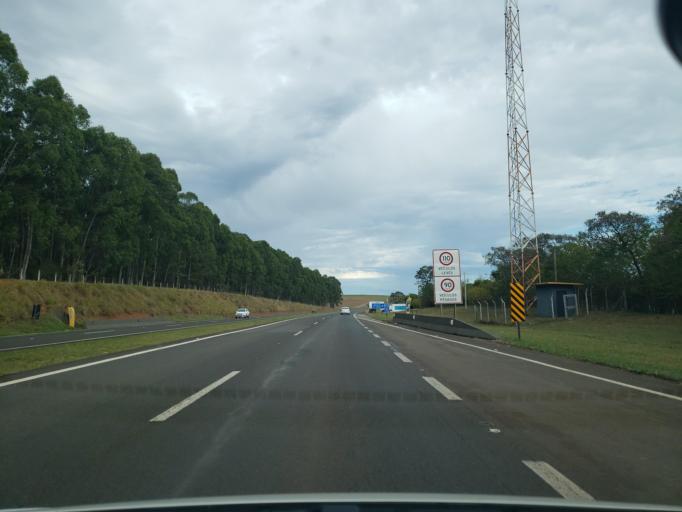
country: BR
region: Sao Paulo
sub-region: Dois Corregos
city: Dois Corregos
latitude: -22.2680
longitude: -48.3903
